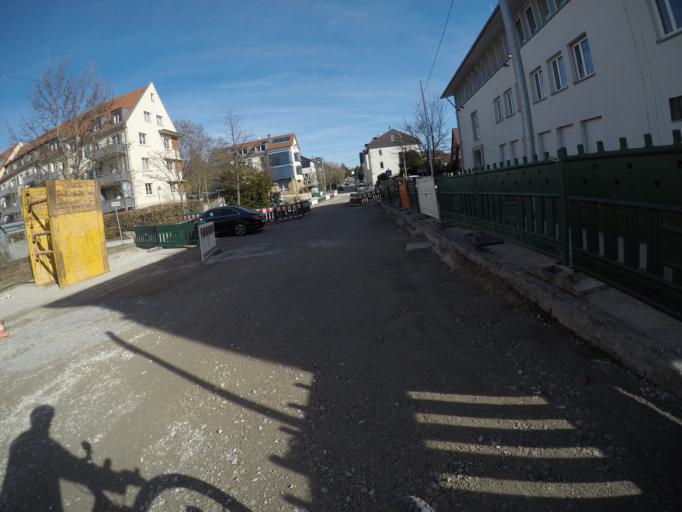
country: DE
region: Baden-Wuerttemberg
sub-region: Regierungsbezirk Stuttgart
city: Stuttgart
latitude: 48.7488
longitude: 9.1728
